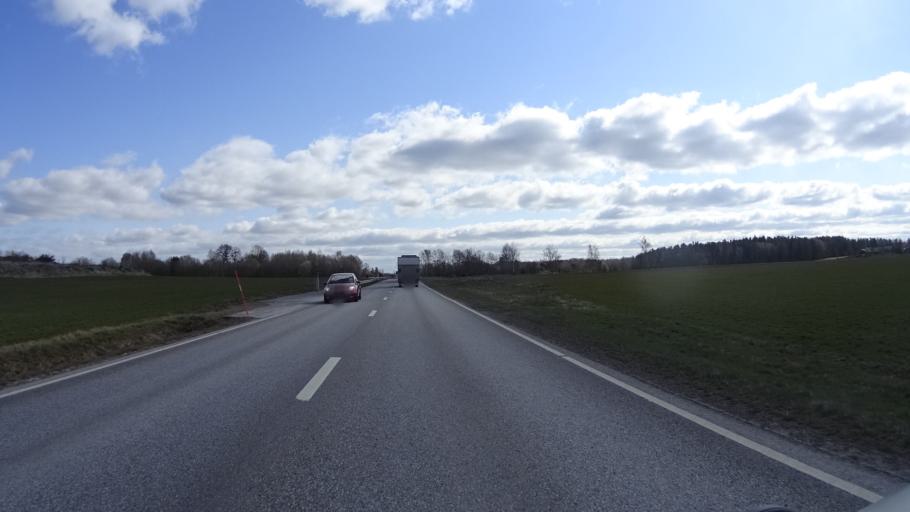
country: SE
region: OEstergoetland
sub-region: Mjolby Kommun
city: Mantorp
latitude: 58.3770
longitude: 15.2637
